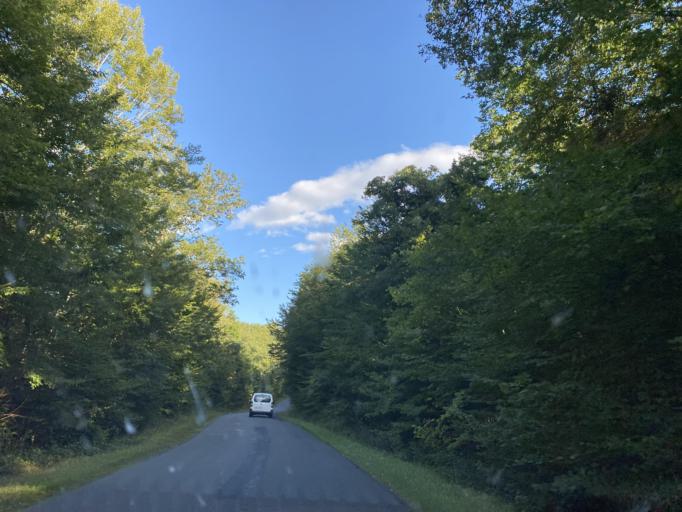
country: FR
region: Auvergne
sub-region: Departement du Puy-de-Dome
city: Randan
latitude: 46.0375
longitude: 3.3294
